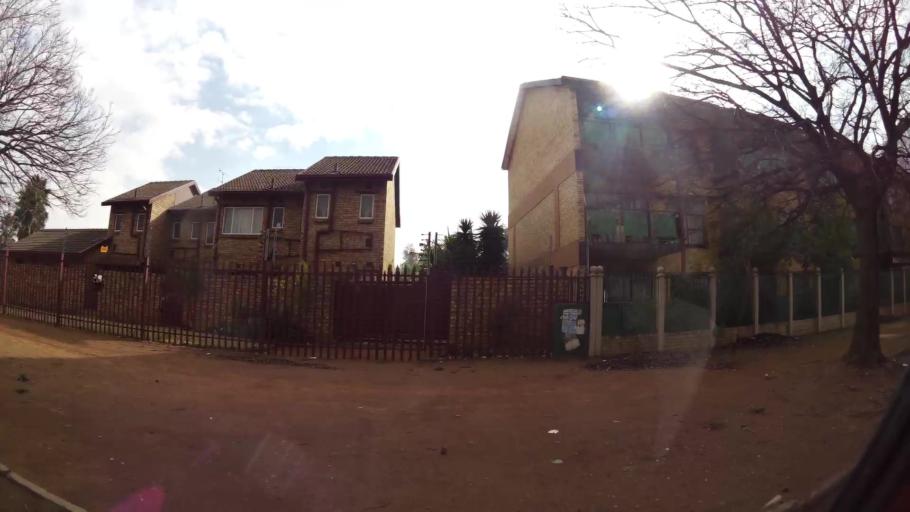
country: ZA
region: Gauteng
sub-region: Sedibeng District Municipality
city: Vanderbijlpark
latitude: -26.6927
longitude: 27.8366
